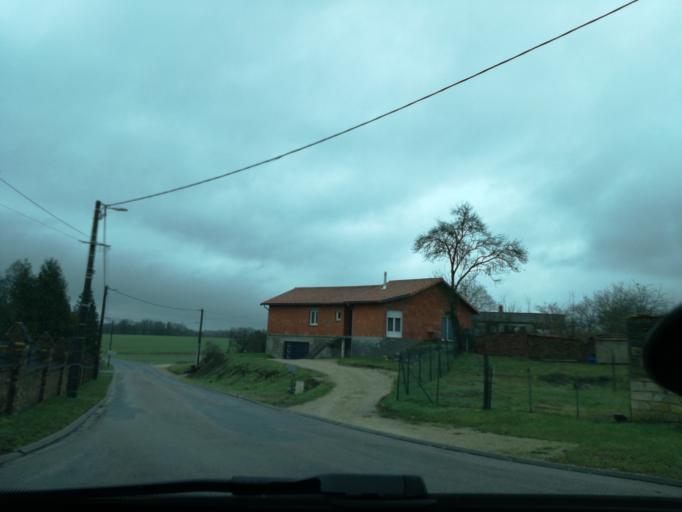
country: FR
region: Lorraine
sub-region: Departement de la Meuse
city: Fains-Veel
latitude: 48.8664
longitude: 5.0787
